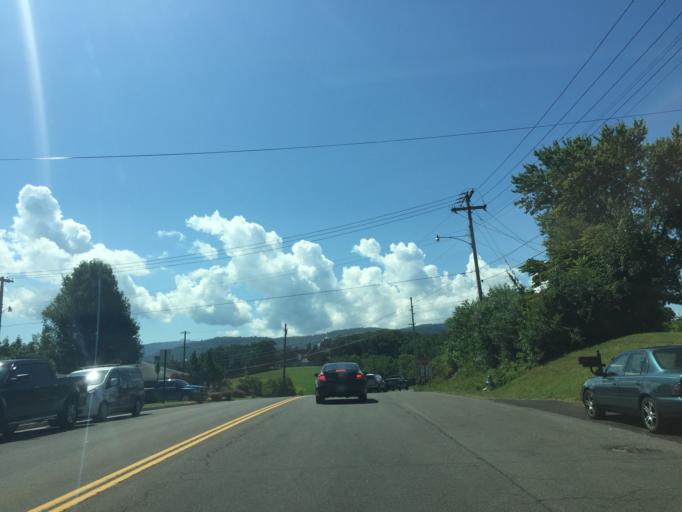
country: US
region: Virginia
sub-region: Warren County
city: Front Royal
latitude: 38.9288
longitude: -78.1989
